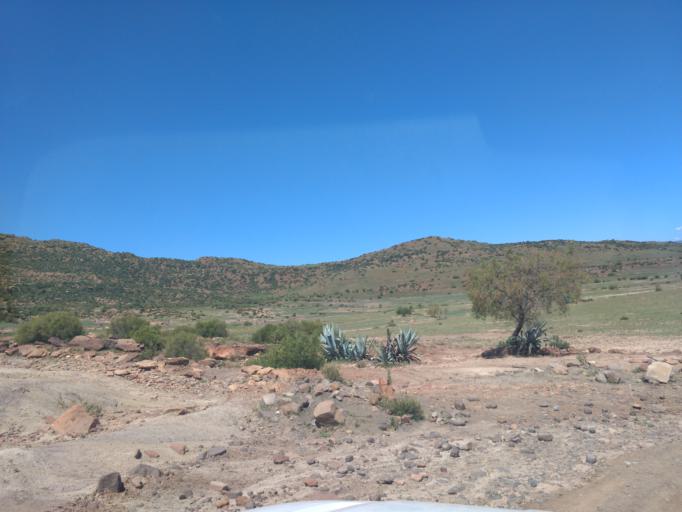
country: LS
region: Maseru
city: Maseru
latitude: -29.4595
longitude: 27.3744
